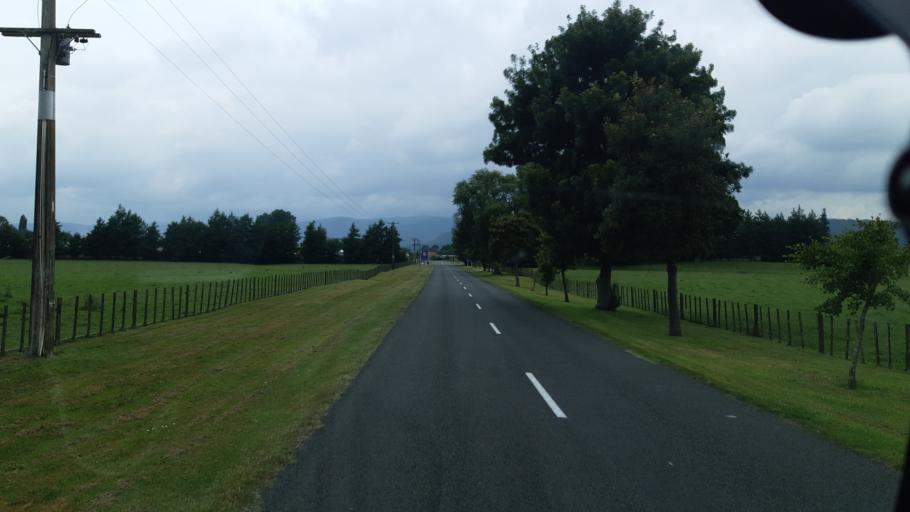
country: NZ
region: Waikato
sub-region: South Waikato District
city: Tokoroa
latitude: -38.3753
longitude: 175.7661
